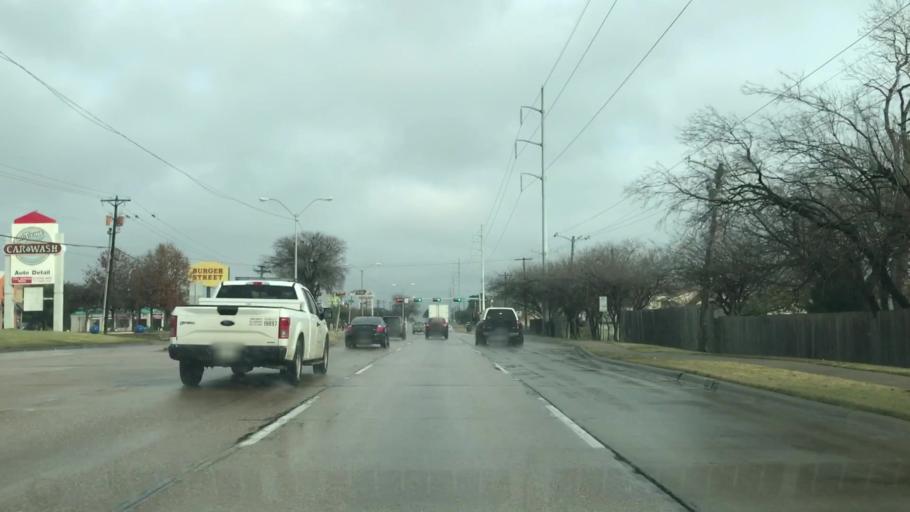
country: US
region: Texas
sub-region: Dallas County
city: Irving
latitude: 32.8497
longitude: -96.9922
